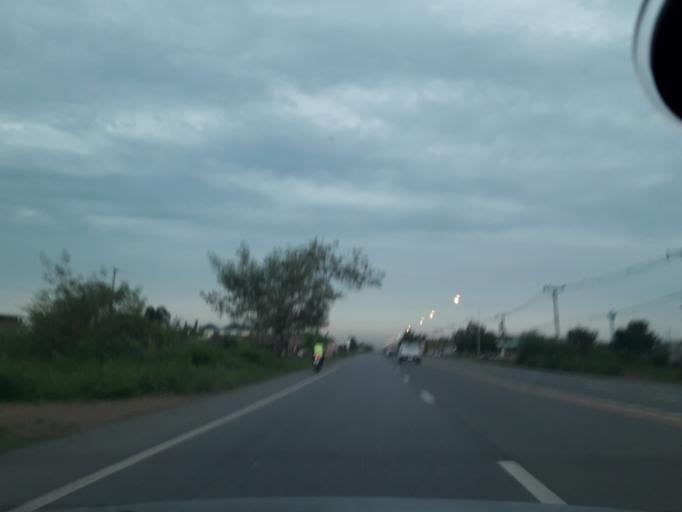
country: TH
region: Pathum Thani
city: Nong Suea
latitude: 14.1224
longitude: 100.7473
